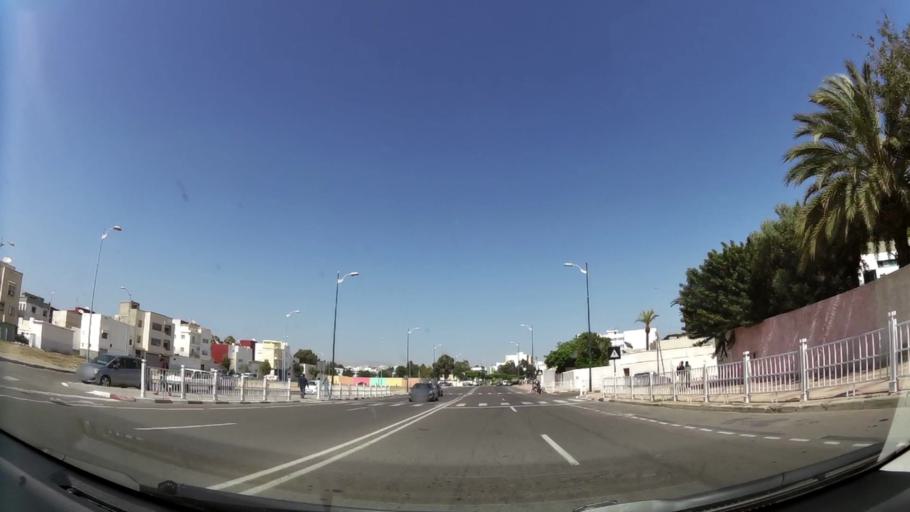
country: MA
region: Souss-Massa-Draa
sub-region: Agadir-Ida-ou-Tnan
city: Agadir
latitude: 30.4087
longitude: -9.5865
